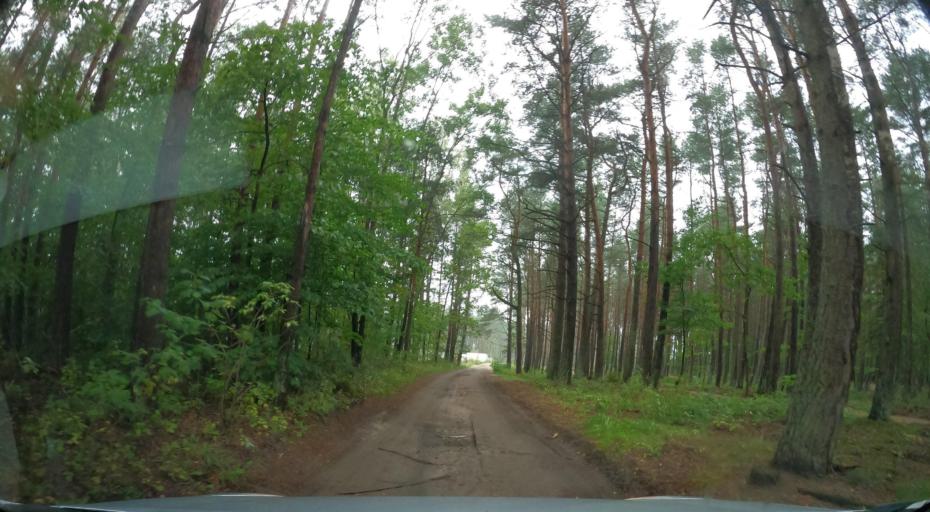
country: PL
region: Pomeranian Voivodeship
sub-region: Powiat kartuski
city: Chwaszczyno
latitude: 54.4351
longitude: 18.4174
